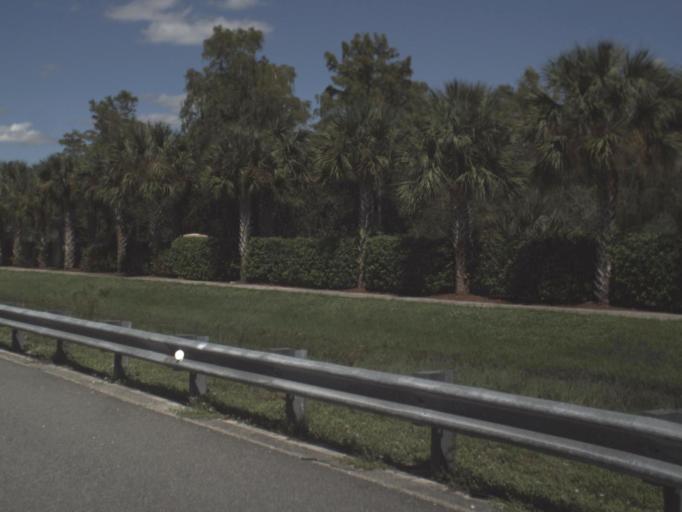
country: US
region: Florida
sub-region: Collier County
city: Lely Resort
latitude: 26.0406
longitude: -81.6635
